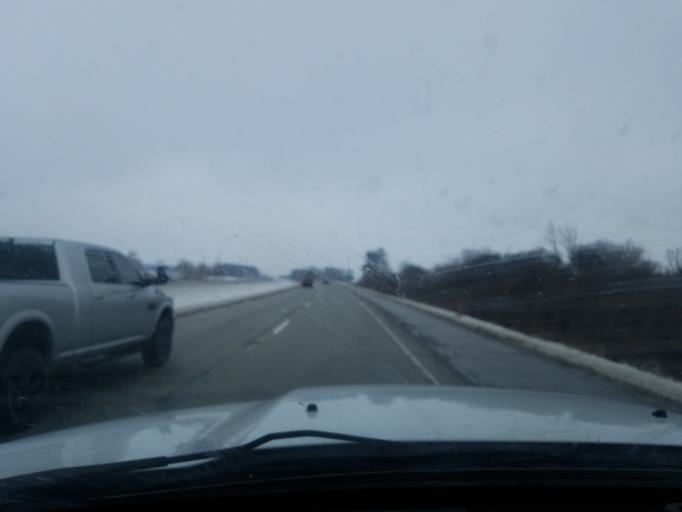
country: US
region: Indiana
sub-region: Marshall County
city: Argos
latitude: 41.1695
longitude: -86.2404
